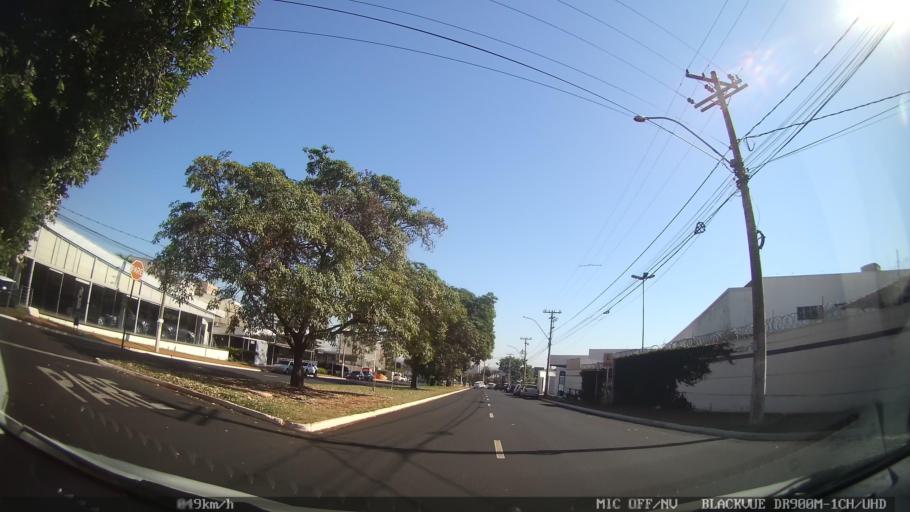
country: BR
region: Sao Paulo
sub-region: Ribeirao Preto
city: Ribeirao Preto
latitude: -21.2104
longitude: -47.8112
